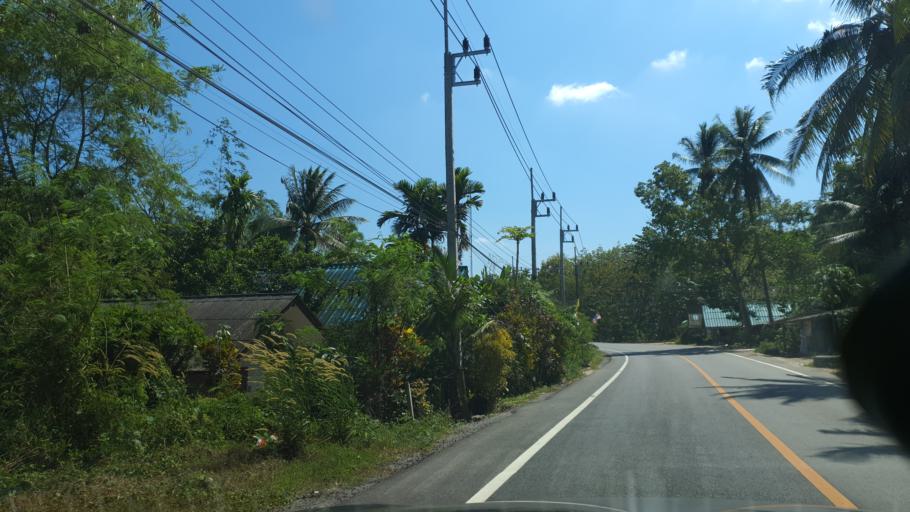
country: TH
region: Krabi
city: Khlong Thom
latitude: 7.9263
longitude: 99.2418
